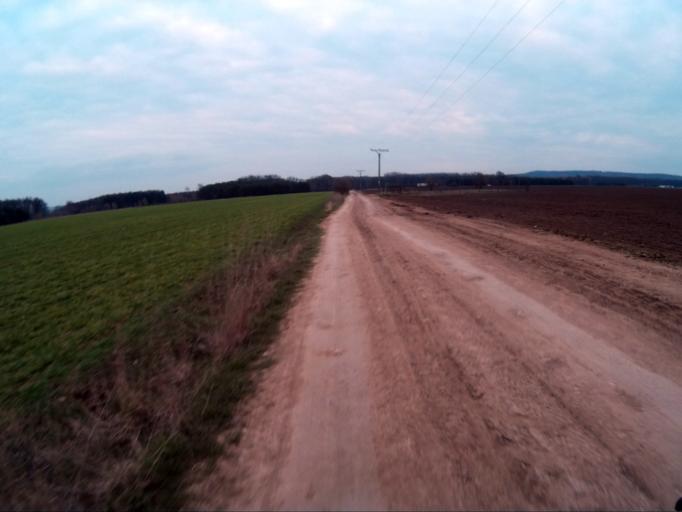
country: CZ
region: South Moravian
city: Nosislav
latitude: 48.9856
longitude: 16.6371
